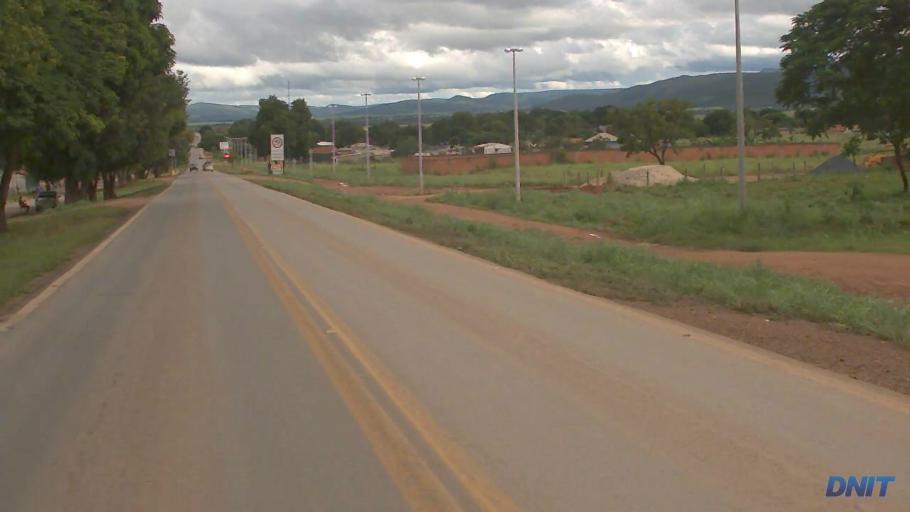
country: BR
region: Goias
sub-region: Padre Bernardo
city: Padre Bernardo
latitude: -15.2560
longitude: -48.2669
